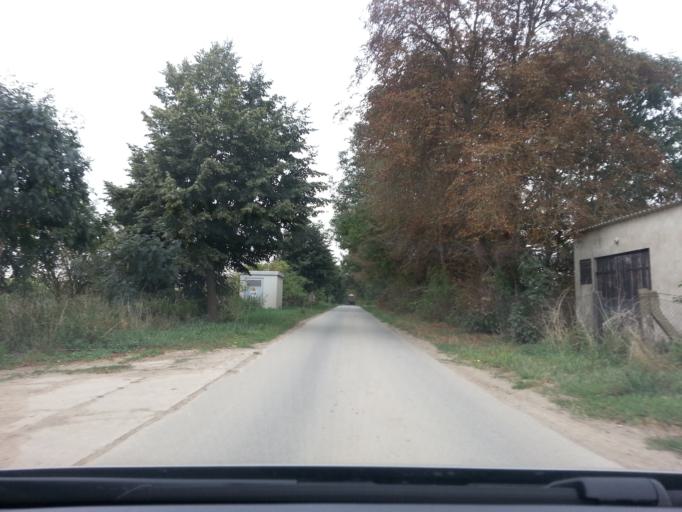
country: DE
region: Mecklenburg-Vorpommern
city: Ferdinandshof
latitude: 53.6647
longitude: 13.9172
